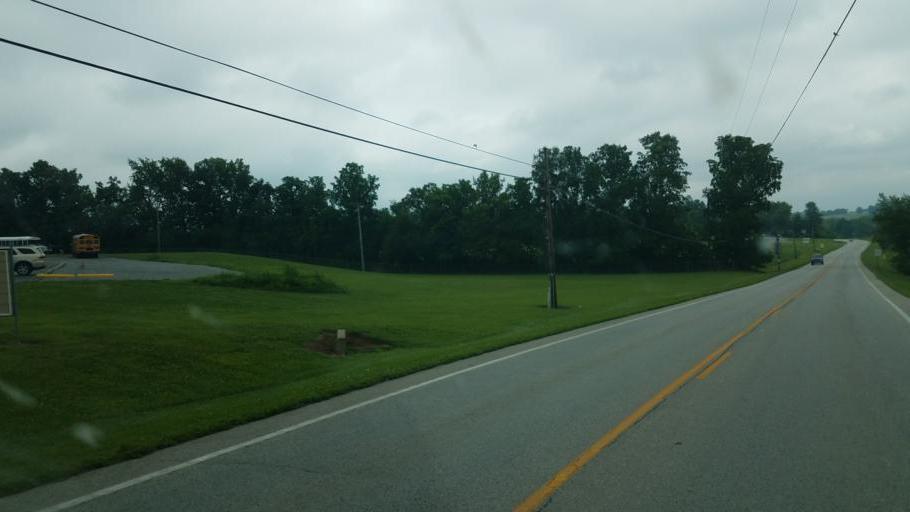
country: US
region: Ohio
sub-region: Highland County
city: Hillsboro
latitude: 39.2106
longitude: -83.5614
